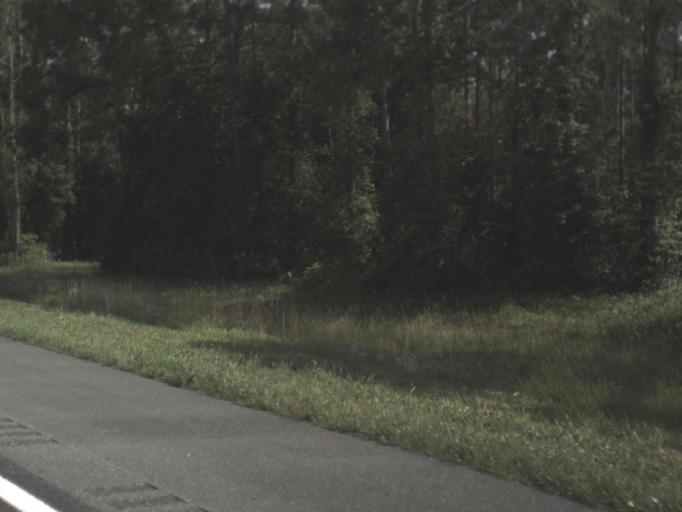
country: US
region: Florida
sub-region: Baker County
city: Macclenny
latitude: 30.2418
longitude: -82.3091
